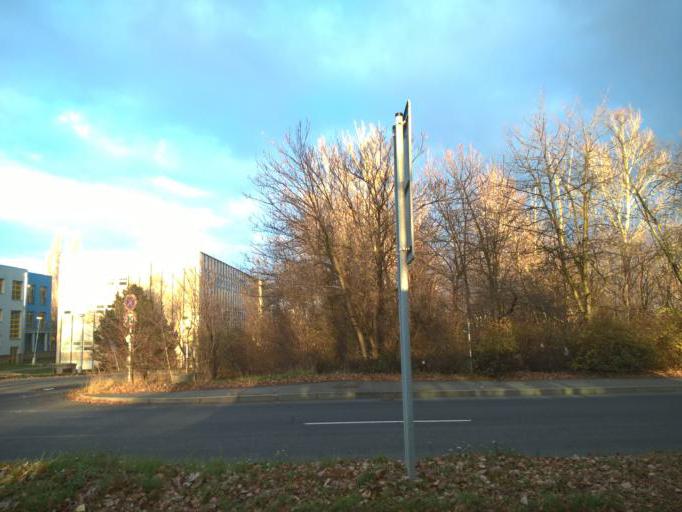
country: CZ
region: Central Bohemia
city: Hostivice
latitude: 50.0954
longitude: 14.2937
